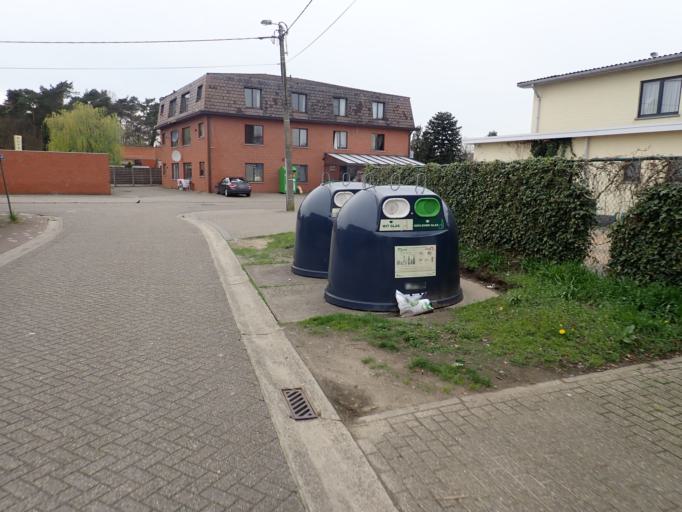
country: BE
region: Flanders
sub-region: Provincie Antwerpen
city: Grobbendonk
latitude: 51.1947
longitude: 4.7207
